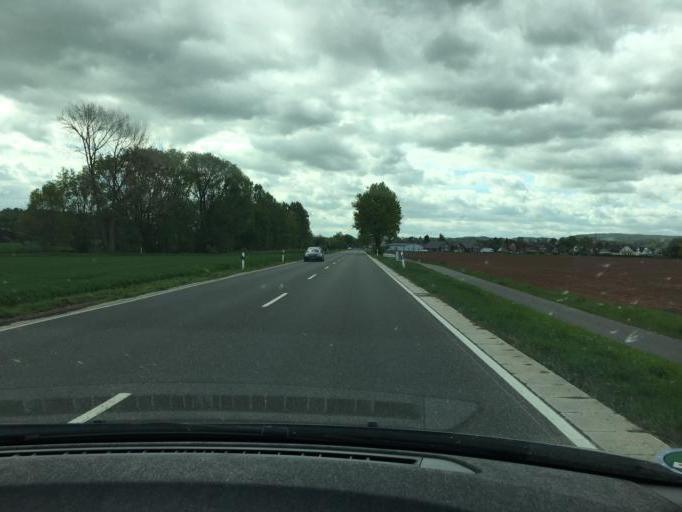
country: DE
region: North Rhine-Westphalia
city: Zulpich
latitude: 50.6533
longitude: 6.6479
